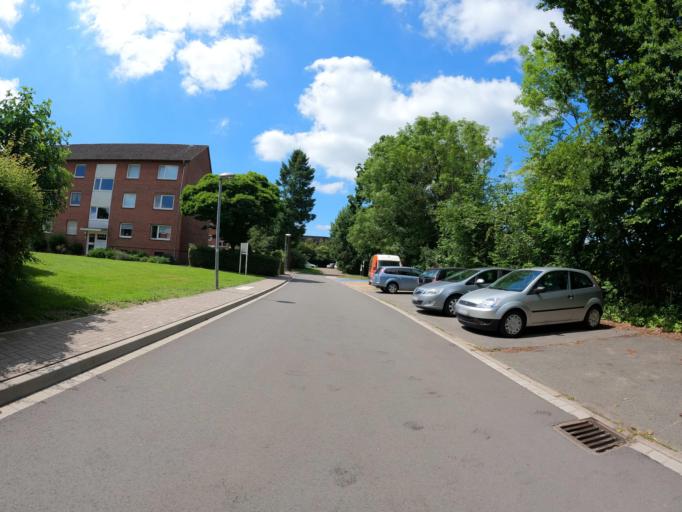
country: DE
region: Schleswig-Holstein
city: Wentorf bei Hamburg
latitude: 53.4969
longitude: 10.2609
